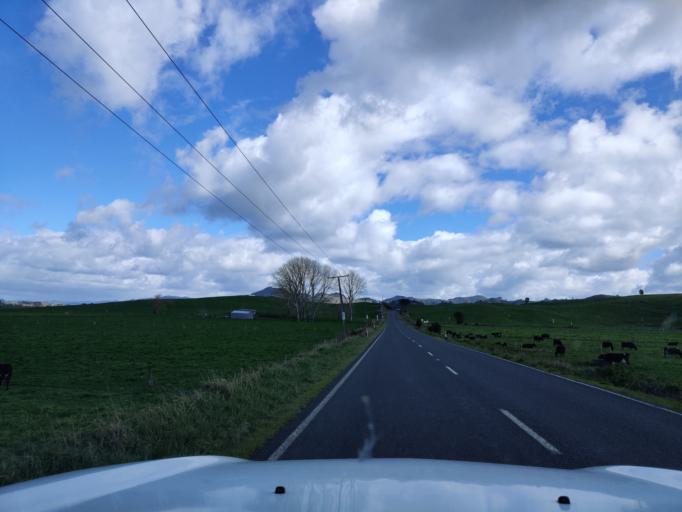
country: NZ
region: Waikato
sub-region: Waikato District
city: Ngaruawahia
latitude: -37.5755
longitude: 175.2388
